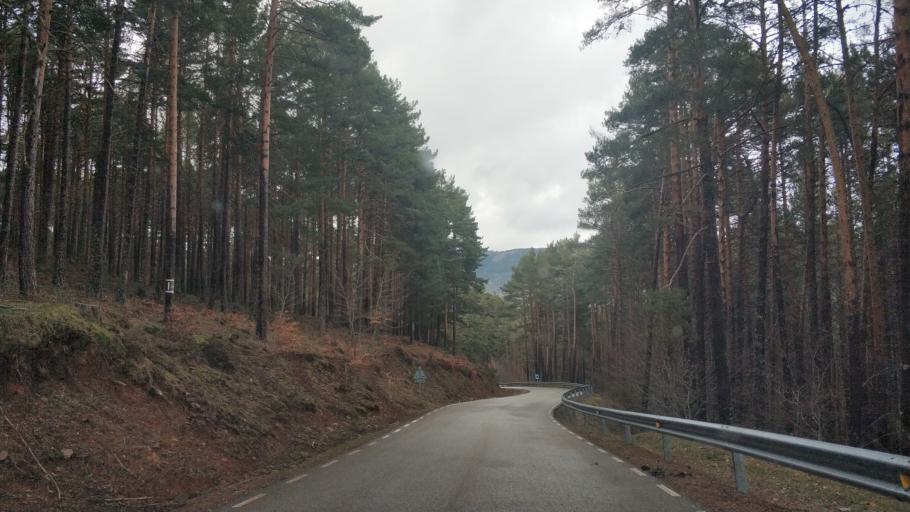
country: ES
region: Castille and Leon
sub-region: Provincia de Burgos
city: Neila
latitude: 42.0510
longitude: -3.0111
